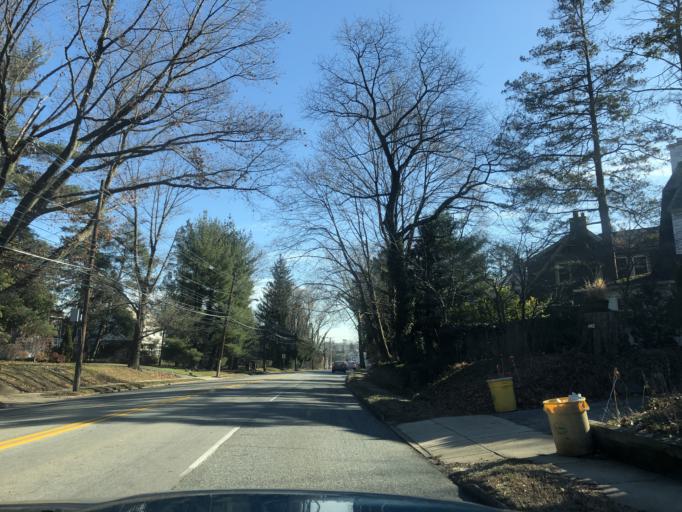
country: US
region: Pennsylvania
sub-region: Montgomery County
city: Narberth
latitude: 40.0131
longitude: -75.2648
